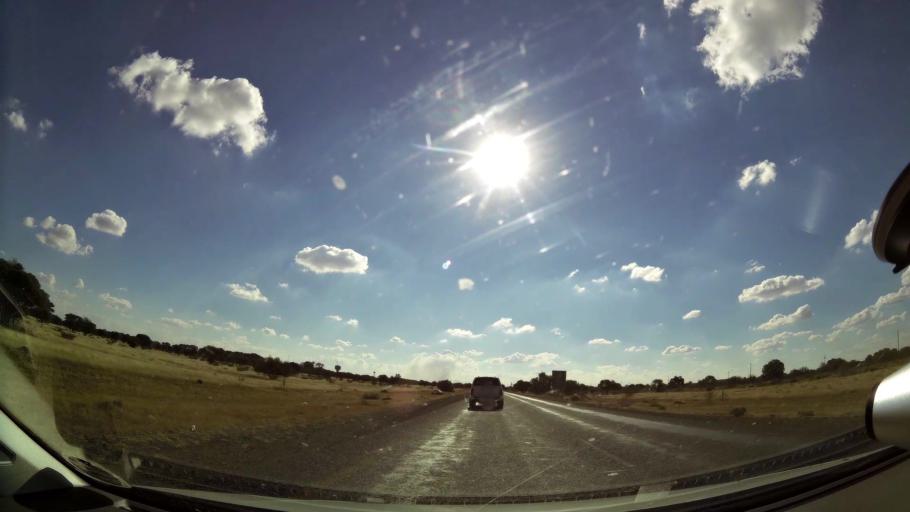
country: ZA
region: Northern Cape
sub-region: Frances Baard District Municipality
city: Kimberley
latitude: -28.7964
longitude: 24.7896
